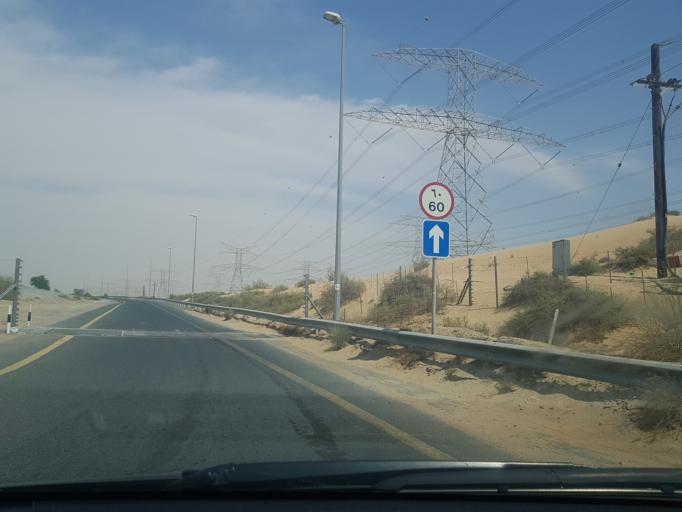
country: AE
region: Ash Shariqah
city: Sharjah
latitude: 25.2085
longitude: 55.5515
